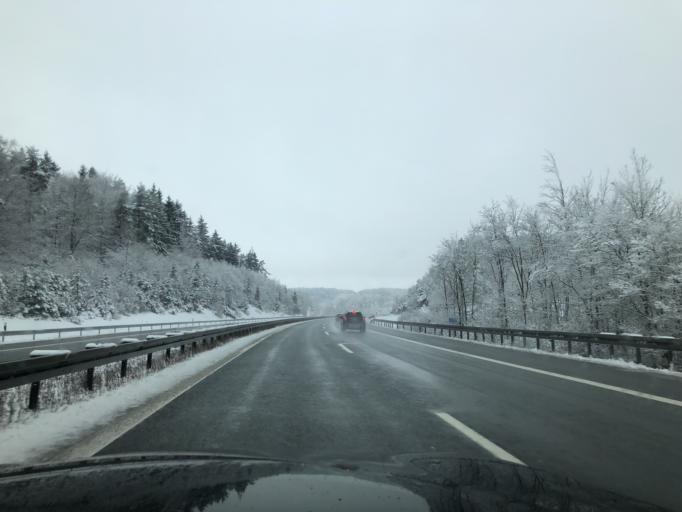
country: DE
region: Bavaria
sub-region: Upper Palatinate
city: Illschwang
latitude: 49.4225
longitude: 11.6317
